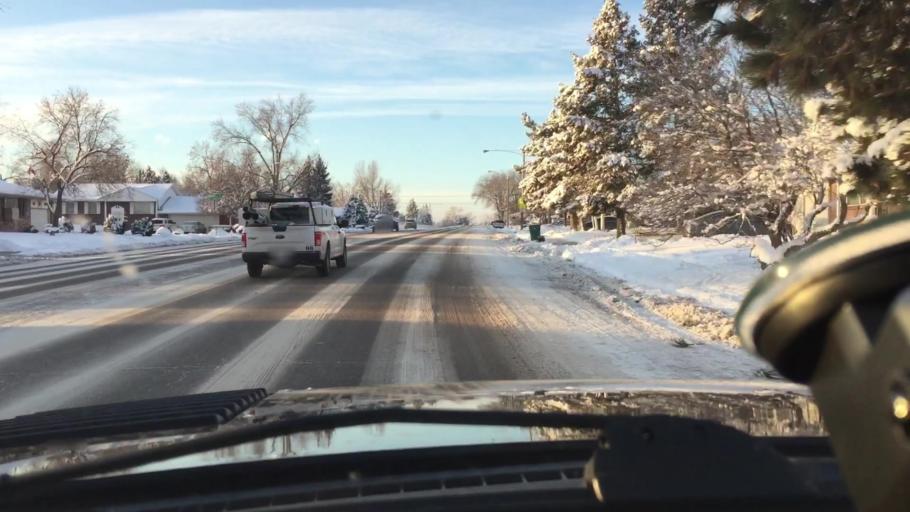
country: US
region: Colorado
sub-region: Adams County
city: Federal Heights
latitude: 39.8466
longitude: -104.9970
